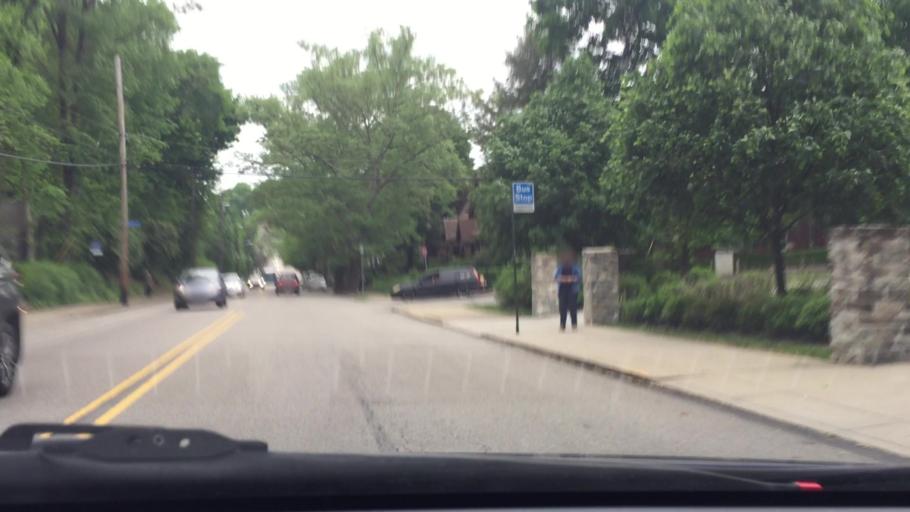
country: US
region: Pennsylvania
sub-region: Allegheny County
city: Bloomfield
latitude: 40.4403
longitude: -79.9354
